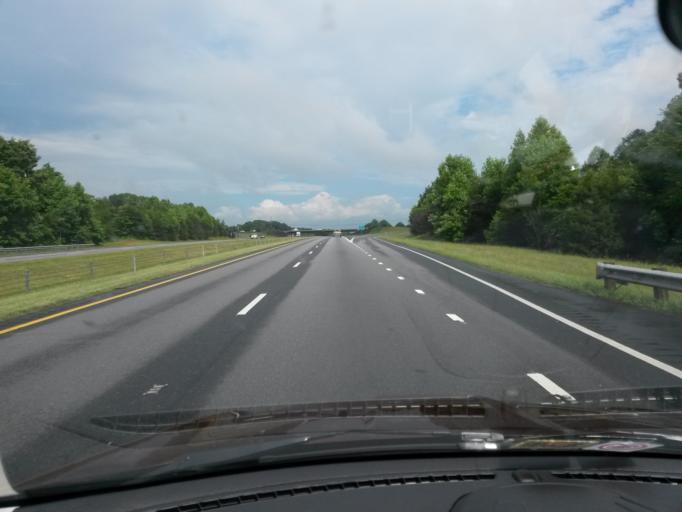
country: US
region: North Carolina
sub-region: Catawba County
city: Maiden
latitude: 35.5939
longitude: -81.2611
